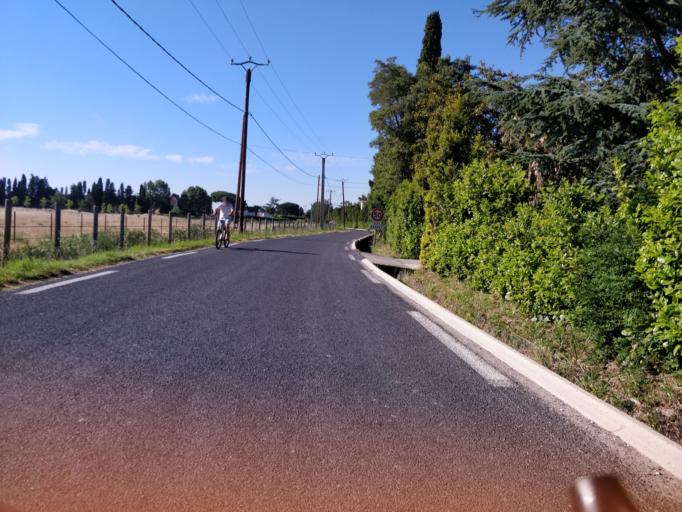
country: FR
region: Languedoc-Roussillon
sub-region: Departement des Pyrenees-Orientales
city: Elne
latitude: 42.6071
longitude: 2.9571
